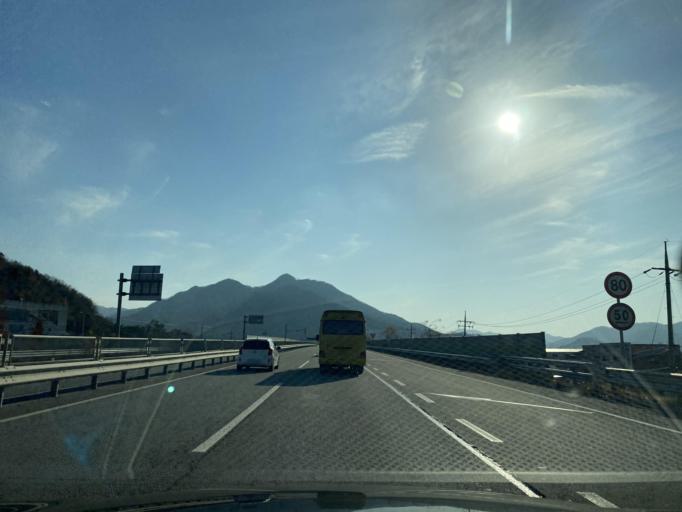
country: KR
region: Chungcheongnam-do
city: Asan
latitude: 36.7657
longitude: 127.0374
